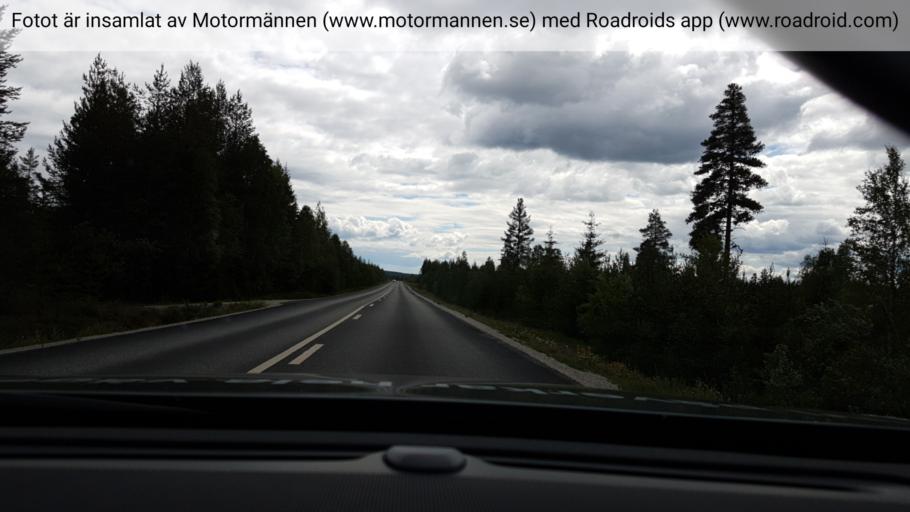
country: SE
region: Vaesterbotten
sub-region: Vindelns Kommun
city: Vindeln
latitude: 64.0721
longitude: 19.6344
